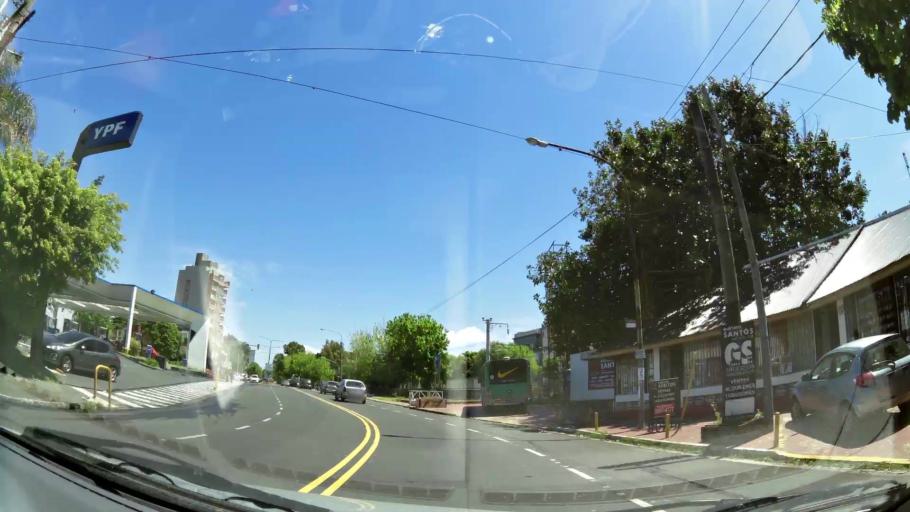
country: AR
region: Buenos Aires
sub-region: Partido de Quilmes
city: Quilmes
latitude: -34.7123
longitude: -58.2745
